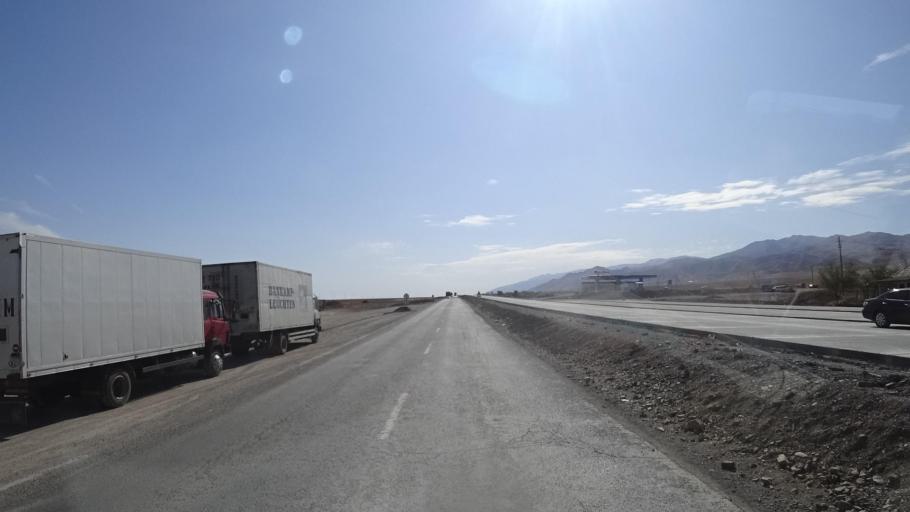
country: KG
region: Chuy
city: Ivanovka
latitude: 43.4005
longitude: 75.1144
